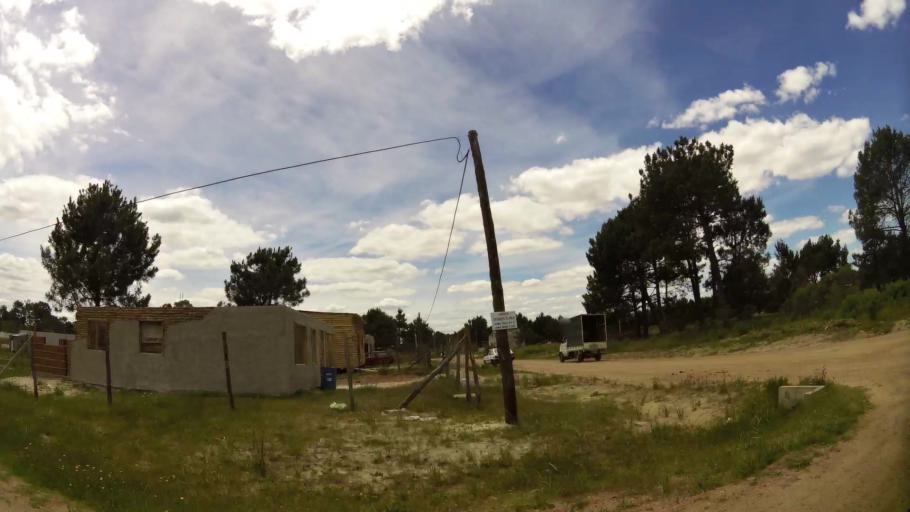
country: UY
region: Canelones
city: Pando
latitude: -34.8067
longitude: -55.9432
